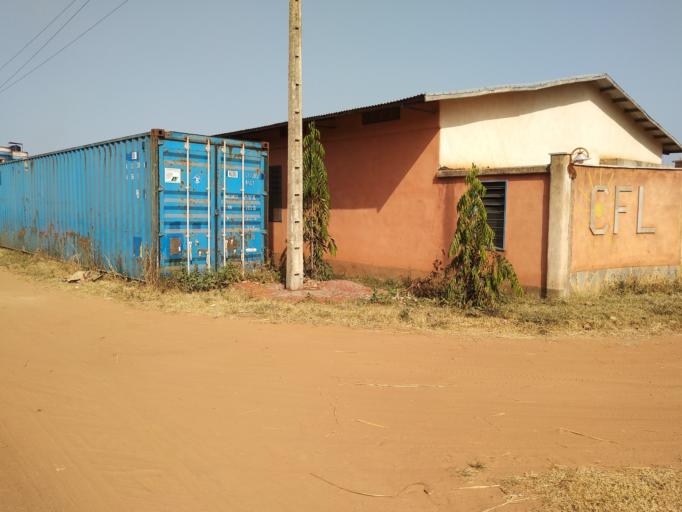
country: BJ
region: Atakora
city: Natitingou
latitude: 10.2756
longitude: 1.3683
